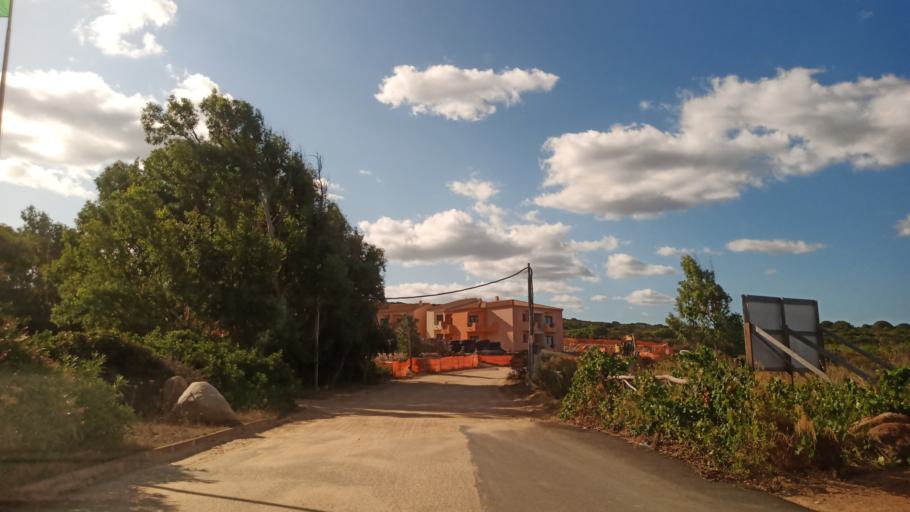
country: IT
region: Sardinia
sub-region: Provincia di Olbia-Tempio
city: Trinita d'Agultu
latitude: 41.0233
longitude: 8.8946
